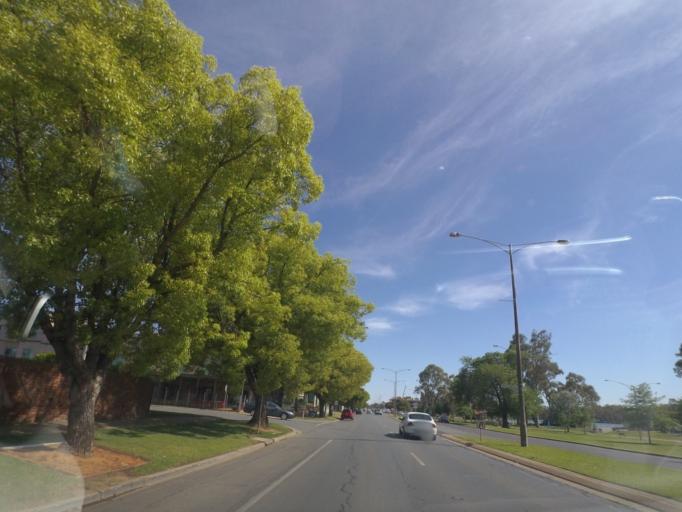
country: AU
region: Victoria
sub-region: Greater Shepparton
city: Shepparton
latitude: -36.3861
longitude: 145.3983
